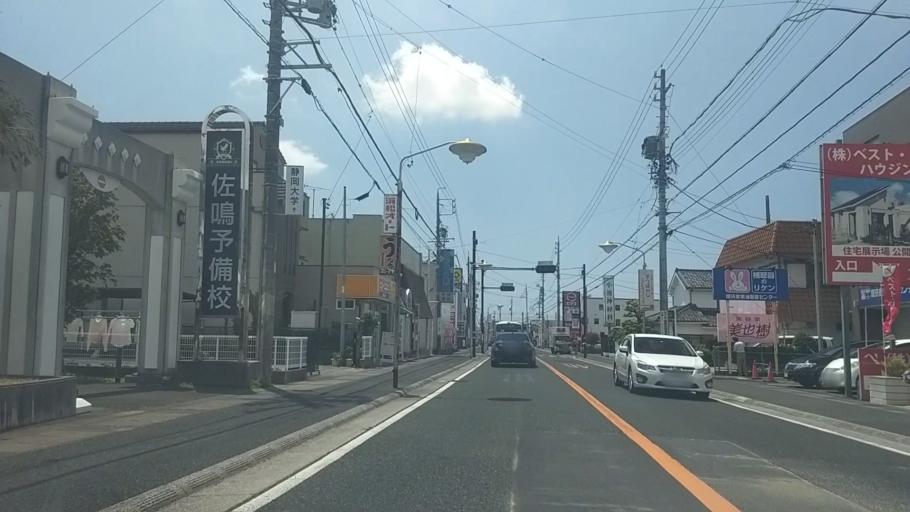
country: JP
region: Shizuoka
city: Hamamatsu
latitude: 34.7409
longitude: 137.7237
